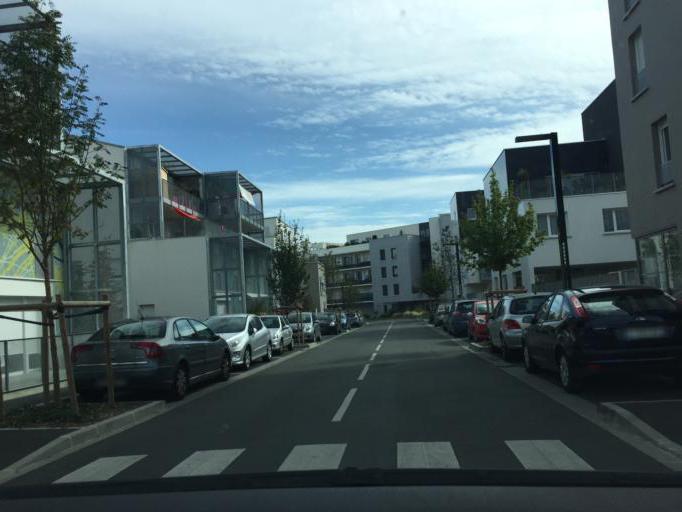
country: FR
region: Ile-de-France
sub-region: Departement de l'Essonne
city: Villebon-sur-Yvette
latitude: 48.7162
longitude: 2.2335
